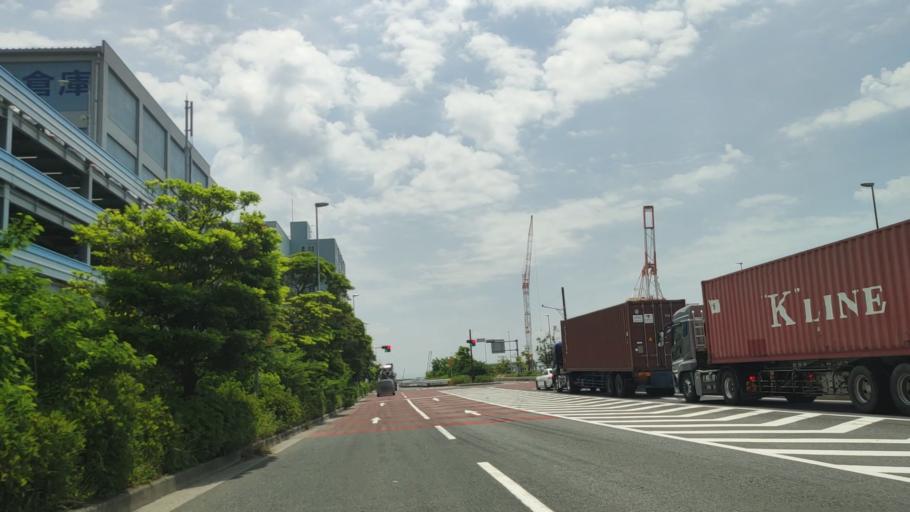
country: JP
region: Kanagawa
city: Yokohama
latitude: 35.4072
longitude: 139.6821
